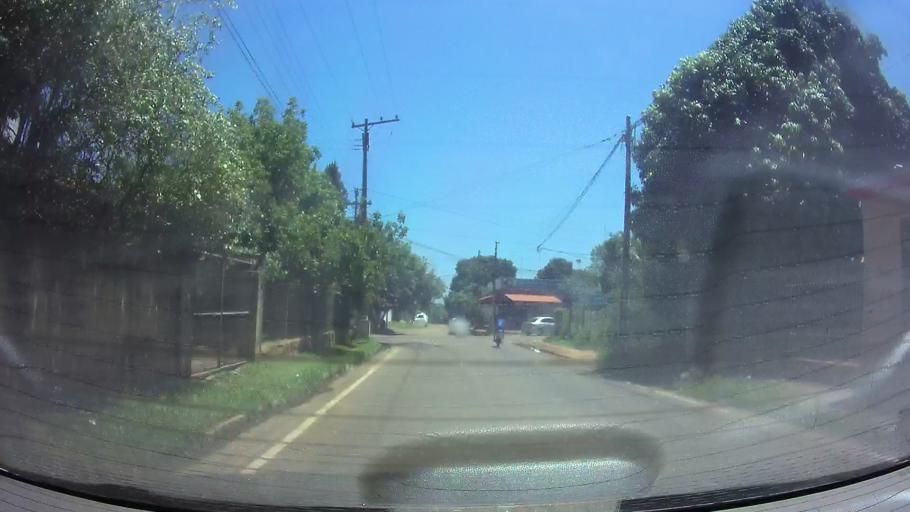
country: PY
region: Central
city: San Lorenzo
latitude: -25.3331
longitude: -57.4842
